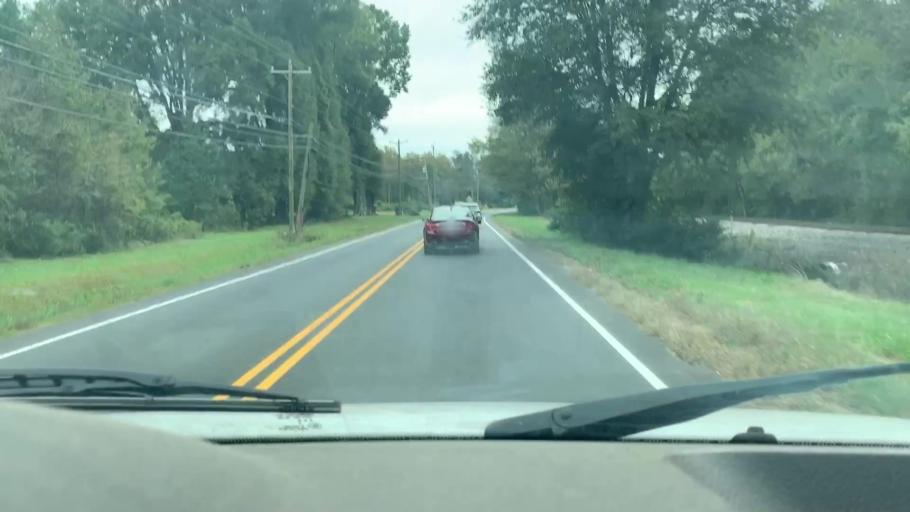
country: US
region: North Carolina
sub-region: Gaston County
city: Davidson
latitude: 35.5139
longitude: -80.8389
